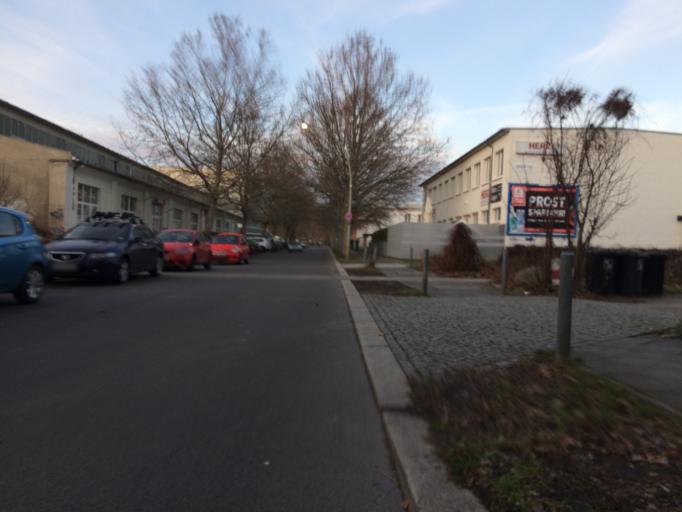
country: DE
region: Berlin
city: Weissensee
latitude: 52.5609
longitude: 13.4612
